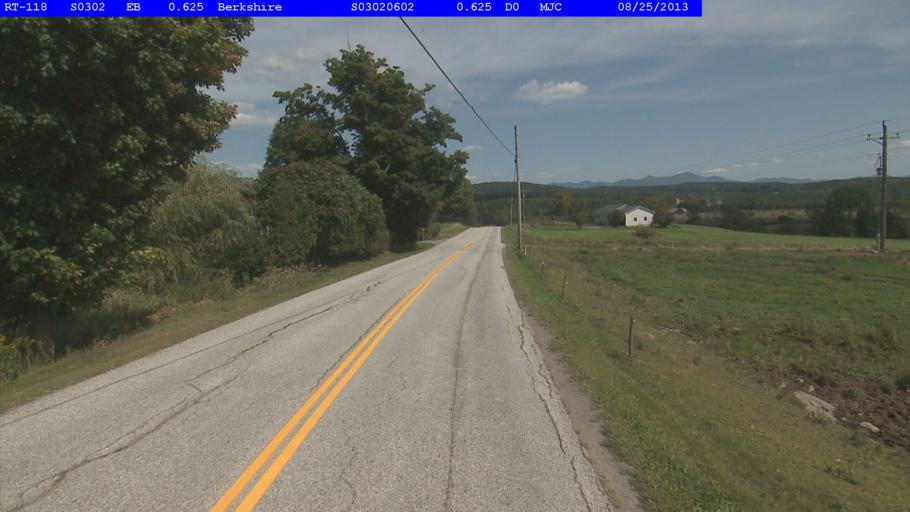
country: US
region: Vermont
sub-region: Franklin County
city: Enosburg Falls
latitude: 44.9841
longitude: -72.8032
